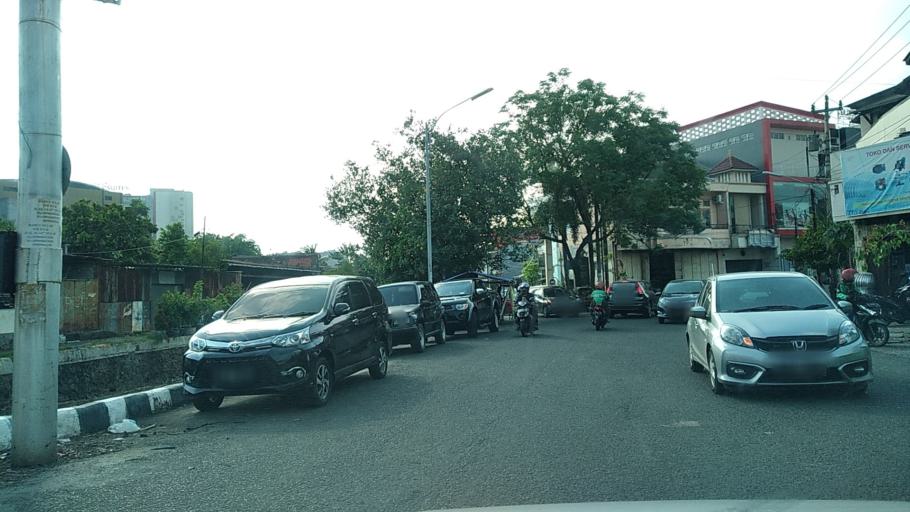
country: ID
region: Central Java
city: Semarang
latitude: -6.9791
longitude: 110.4237
